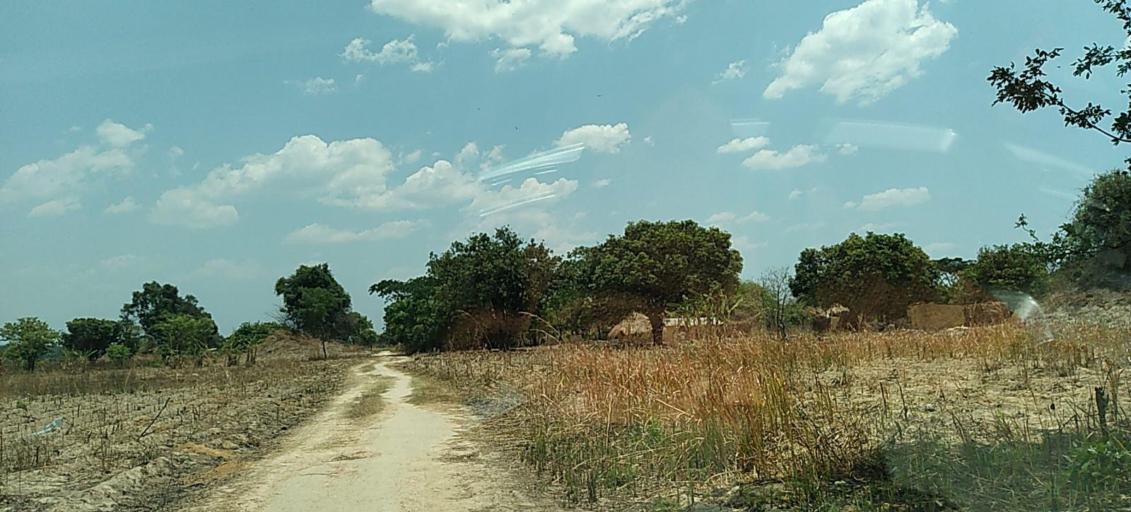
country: ZM
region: Copperbelt
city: Chililabombwe
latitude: -12.4731
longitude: 27.6657
